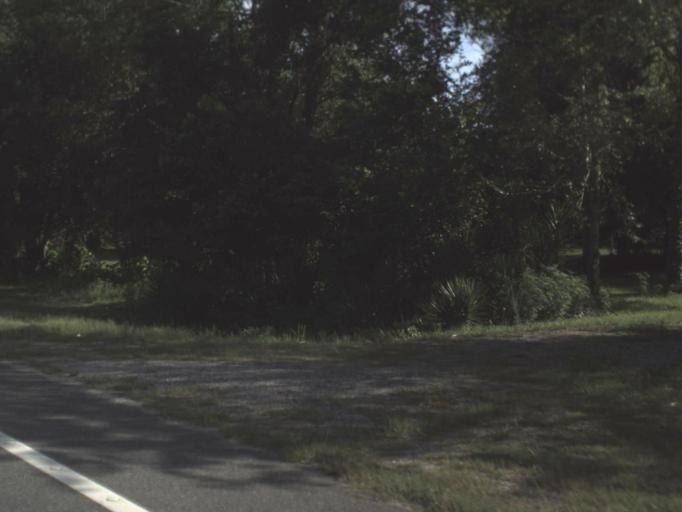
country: US
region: Florida
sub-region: Madison County
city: Madison
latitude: 30.4079
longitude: -83.3663
